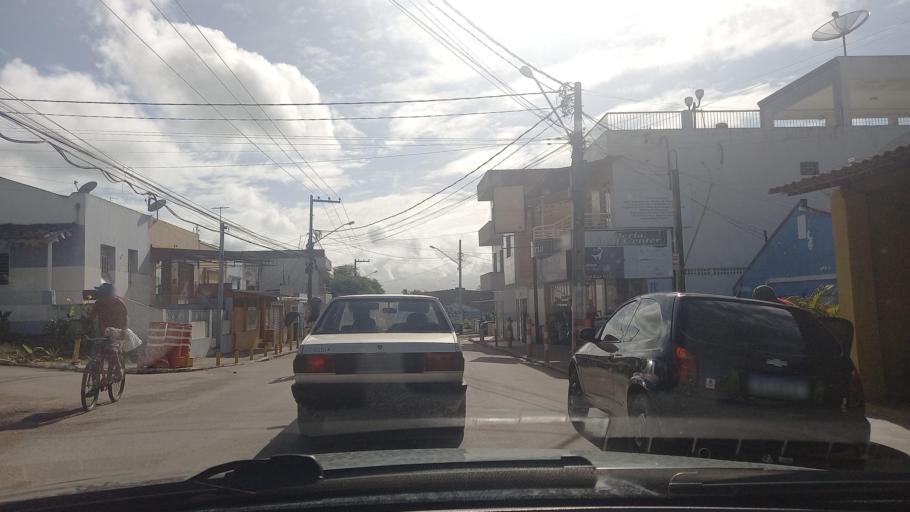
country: BR
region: Pernambuco
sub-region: Vitoria De Santo Antao
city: Vitoria de Santo Antao
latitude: -8.1092
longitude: -35.2863
